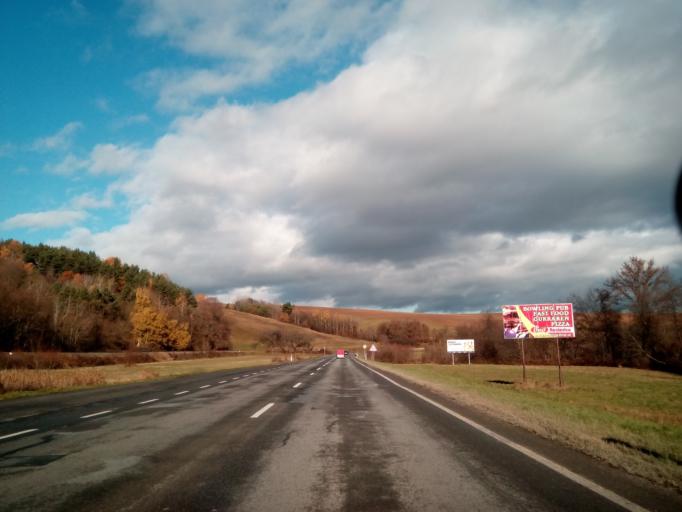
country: SK
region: Presovsky
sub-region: Okres Presov
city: Presov
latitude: 49.1347
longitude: 21.3168
